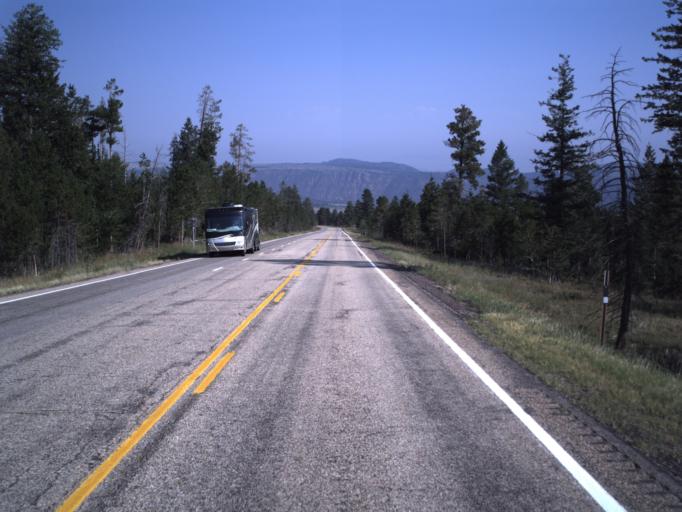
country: US
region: Utah
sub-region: Daggett County
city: Manila
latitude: 40.8557
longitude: -109.4633
